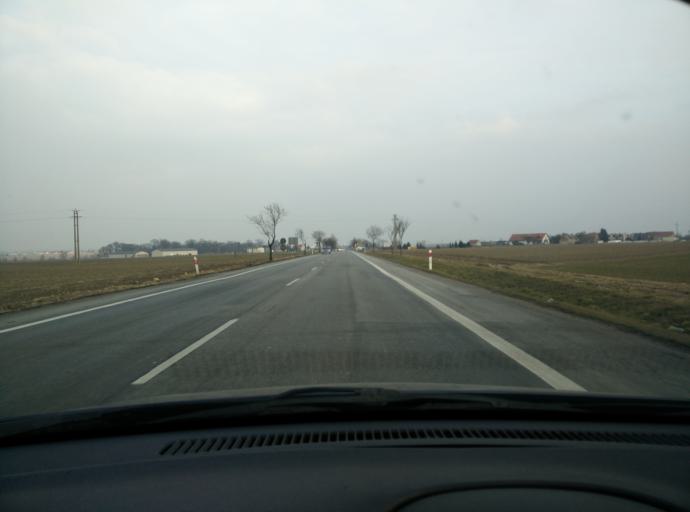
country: PL
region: Greater Poland Voivodeship
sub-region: Powiat sredzki
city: Sroda Wielkopolska
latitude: 52.2291
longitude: 17.2146
